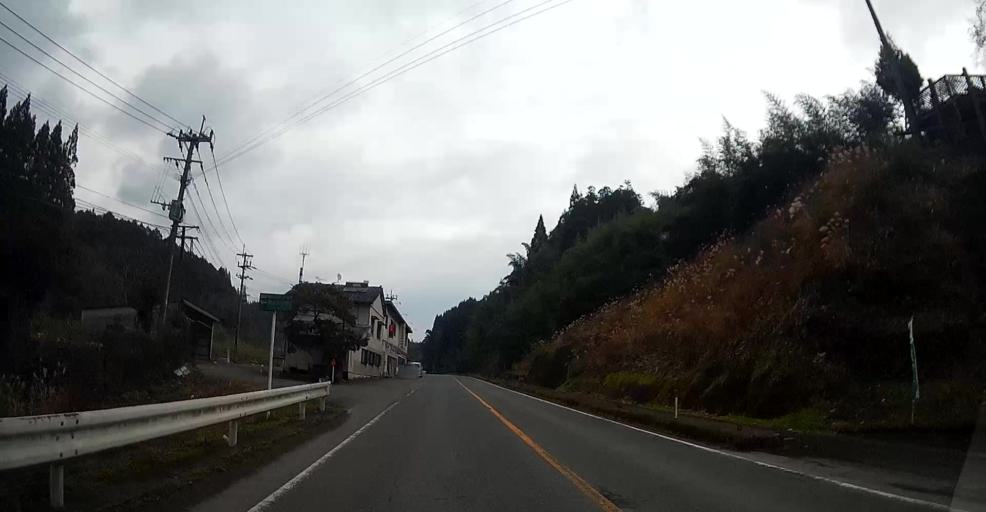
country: JP
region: Kumamoto
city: Matsubase
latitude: 32.6205
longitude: 130.8617
